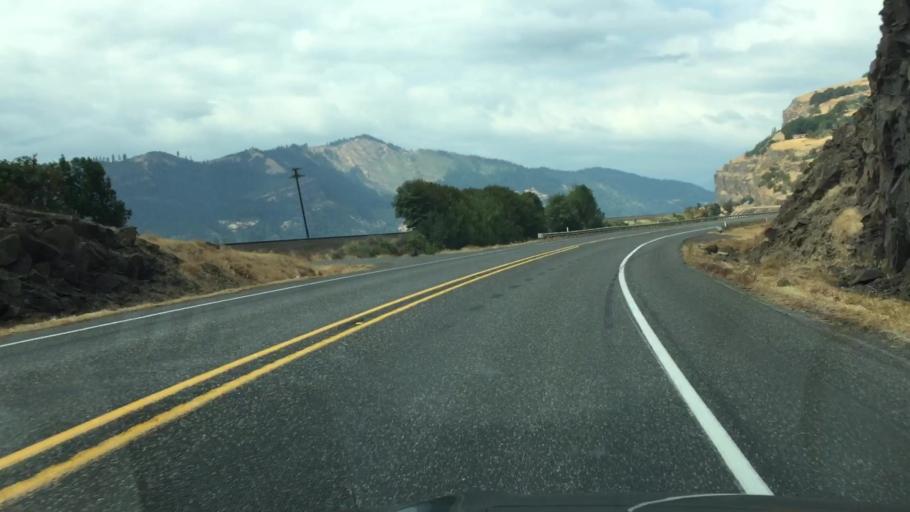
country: US
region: Washington
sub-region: Klickitat County
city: White Salmon
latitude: 45.6980
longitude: -121.3967
